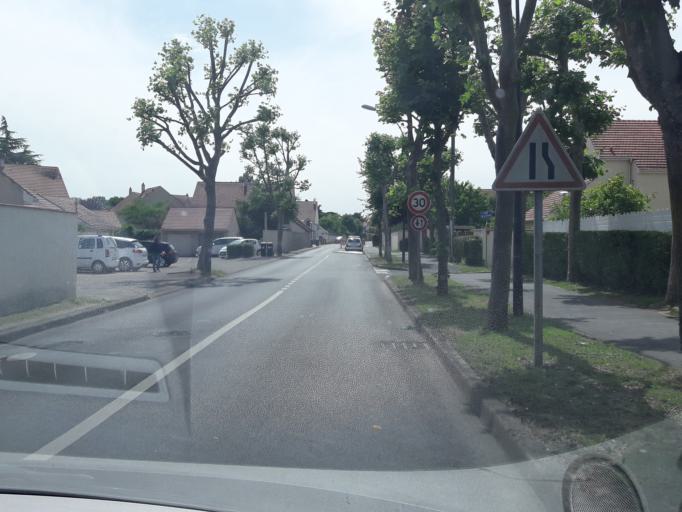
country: FR
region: Ile-de-France
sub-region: Departement de l'Essonne
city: Villemoisson-sur-Orge
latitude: 48.6606
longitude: 2.3335
